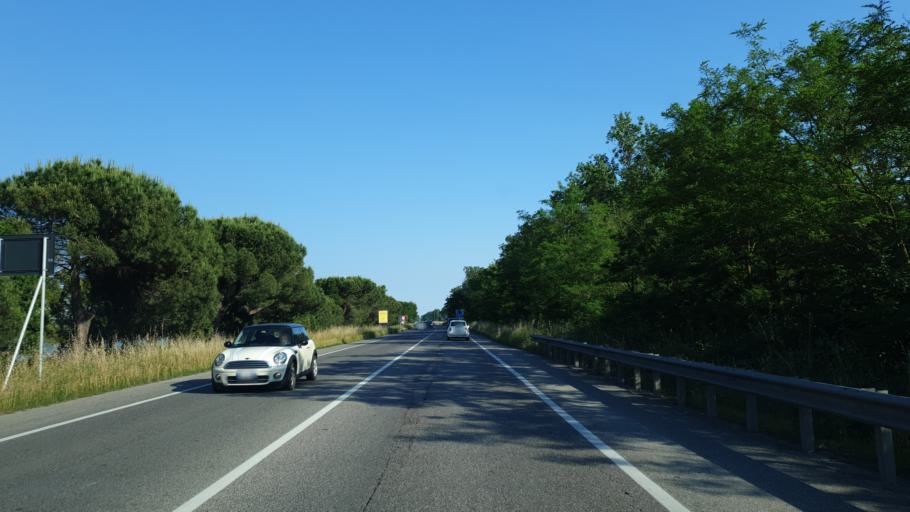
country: IT
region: Emilia-Romagna
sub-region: Provincia di Ravenna
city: Fosso Ghiaia
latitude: 44.3400
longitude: 12.2671
